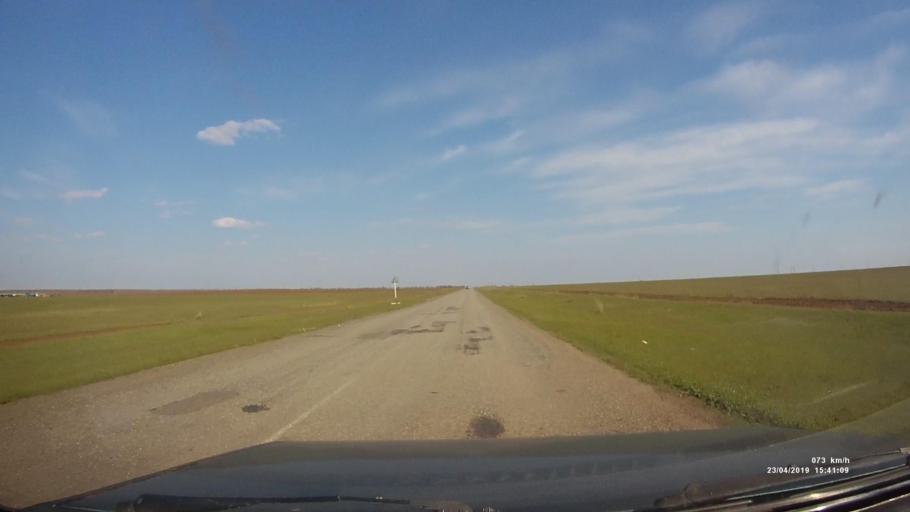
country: RU
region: Rostov
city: Remontnoye
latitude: 46.5525
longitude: 43.0474
